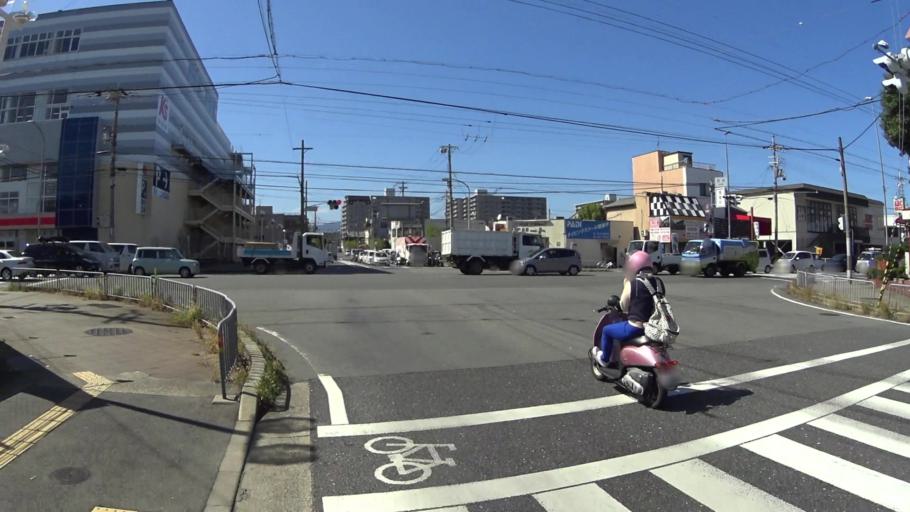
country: JP
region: Kyoto
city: Muko
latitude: 34.9463
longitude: 135.7457
